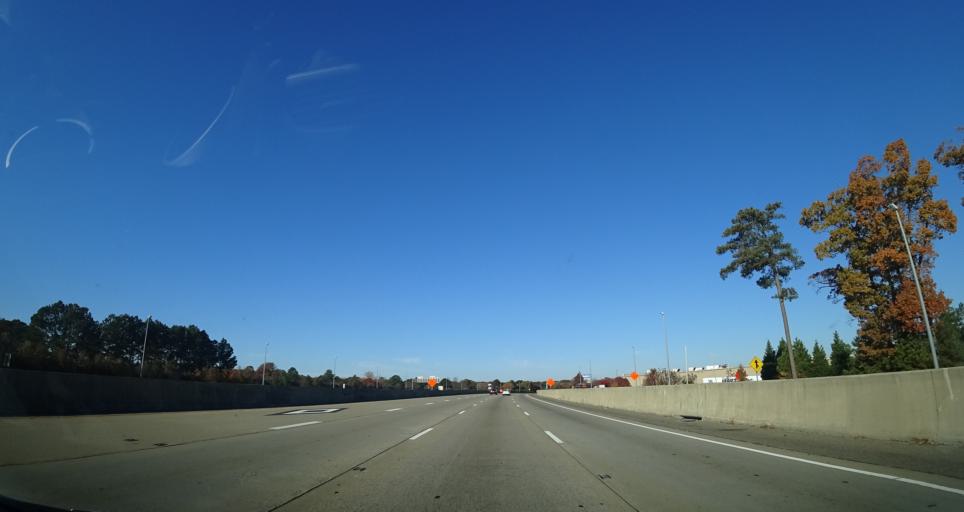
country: US
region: Virginia
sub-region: York County
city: Yorktown
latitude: 37.1169
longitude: -76.5053
